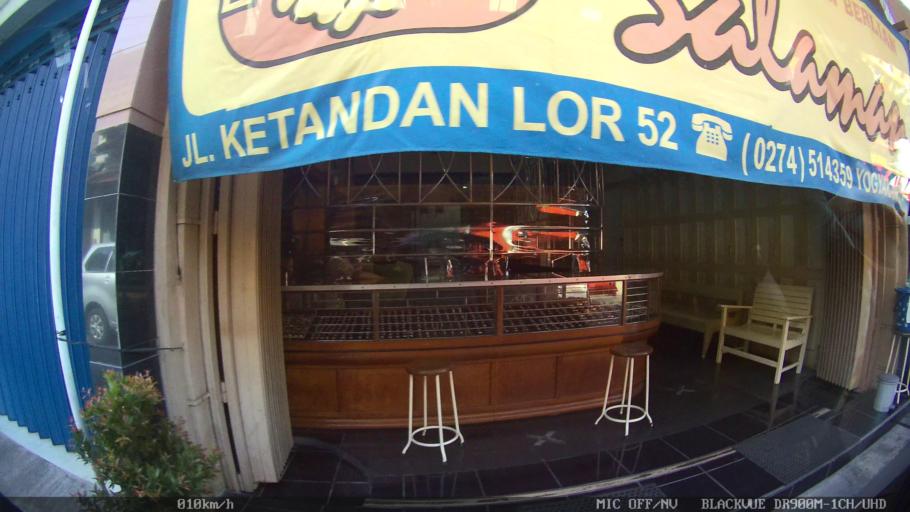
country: ID
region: Daerah Istimewa Yogyakarta
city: Yogyakarta
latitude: -7.7972
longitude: 110.3668
